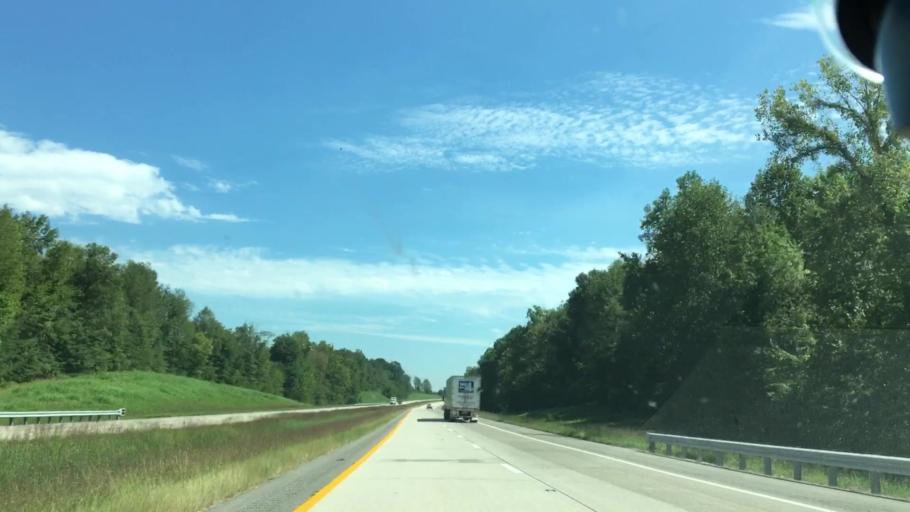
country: US
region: Kentucky
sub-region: Henderson County
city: Henderson
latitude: 37.7766
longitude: -87.4435
